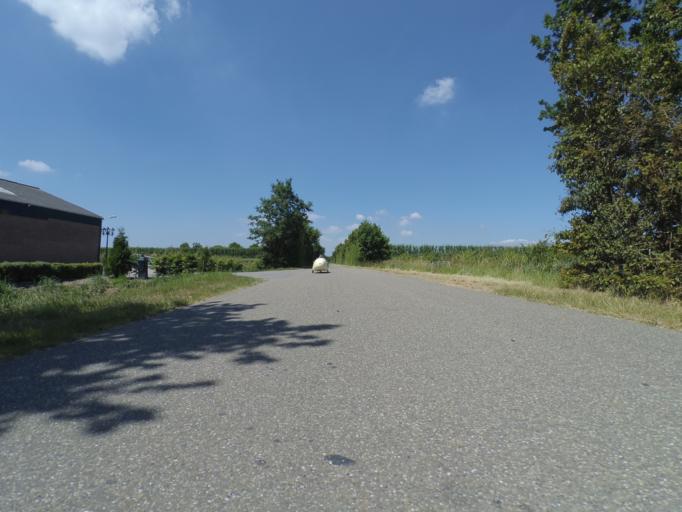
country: NL
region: Zeeland
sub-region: Gemeente Reimerswaal
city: Yerseke
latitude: 51.5536
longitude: 4.0633
